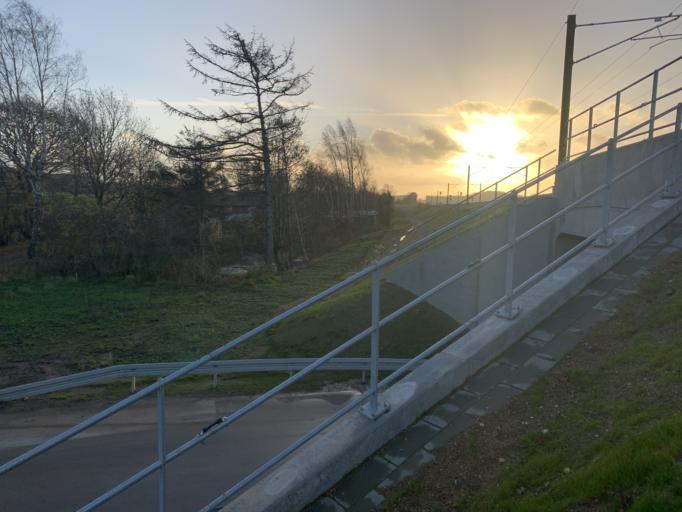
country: DK
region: Zealand
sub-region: Naestved Kommune
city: Fensmark
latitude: 55.3426
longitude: 11.7062
